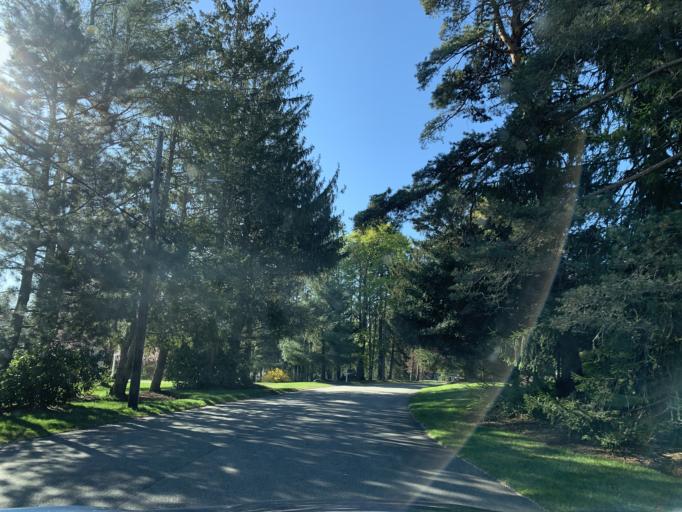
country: US
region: Massachusetts
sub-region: Norfolk County
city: Westwood
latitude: 42.2351
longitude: -71.2142
